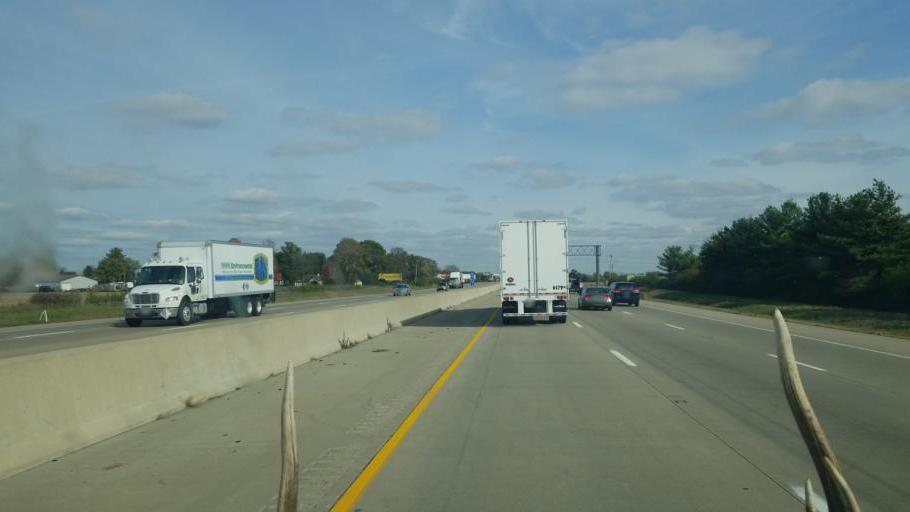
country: US
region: Indiana
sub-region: Marion County
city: Cumberland
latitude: 39.8090
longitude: -85.9463
